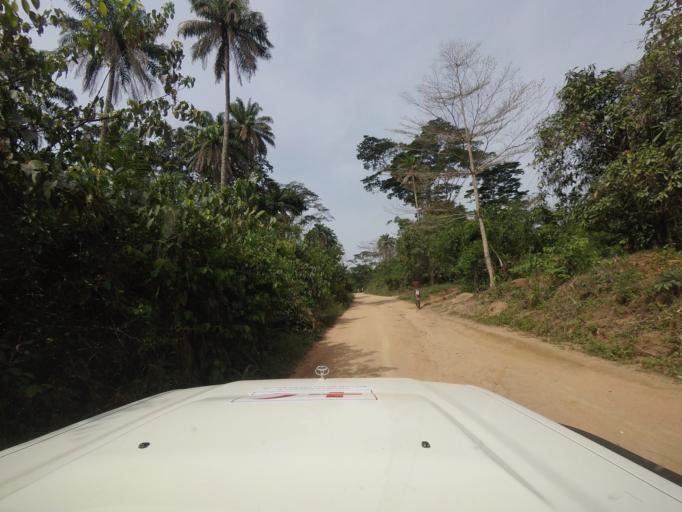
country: GN
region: Nzerekore
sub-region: Macenta
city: Macenta
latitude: 8.4616
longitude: -9.5815
